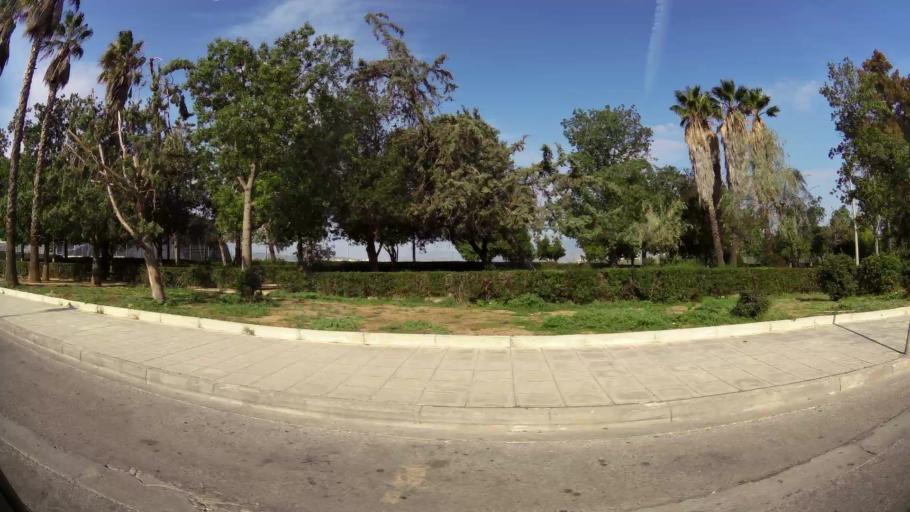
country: GR
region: Attica
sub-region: Nomarchia Athinas
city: Nea Ionia
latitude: 38.0275
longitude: 23.7625
